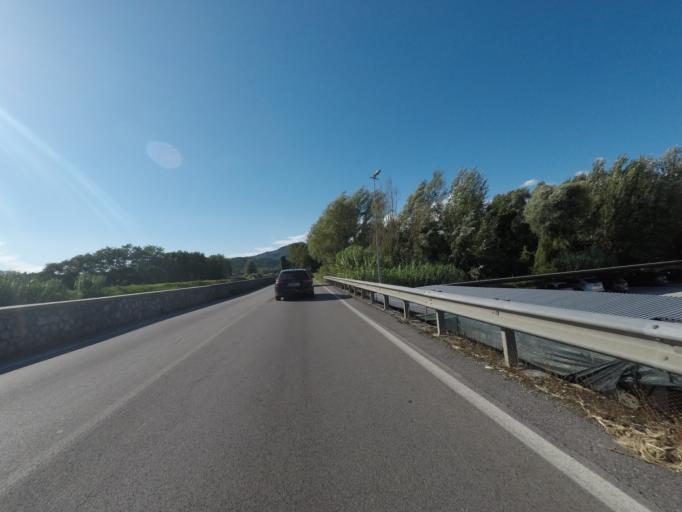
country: IT
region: Tuscany
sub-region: Provincia di Lucca
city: Lucca
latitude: 43.8712
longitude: 10.4992
